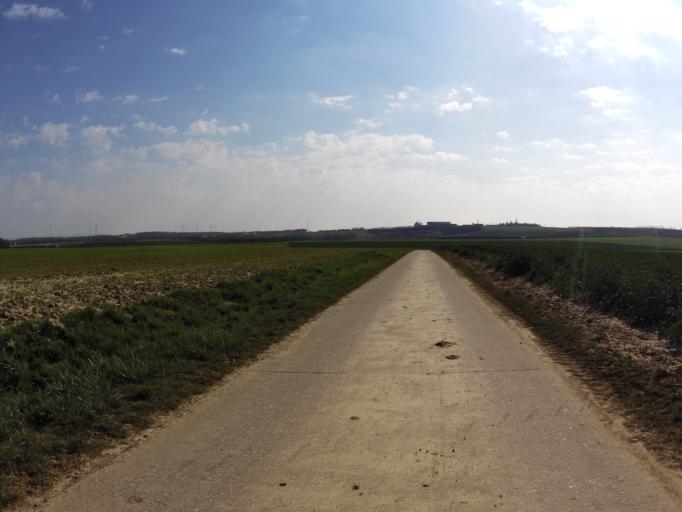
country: DE
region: Bavaria
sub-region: Regierungsbezirk Unterfranken
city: Biebelried
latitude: 49.7994
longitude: 10.0725
